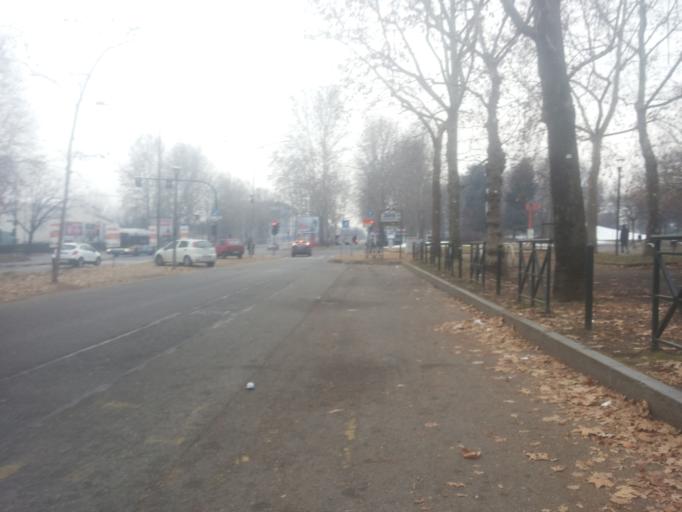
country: IT
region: Piedmont
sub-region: Provincia di Torino
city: Lesna
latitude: 45.0586
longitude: 7.6348
